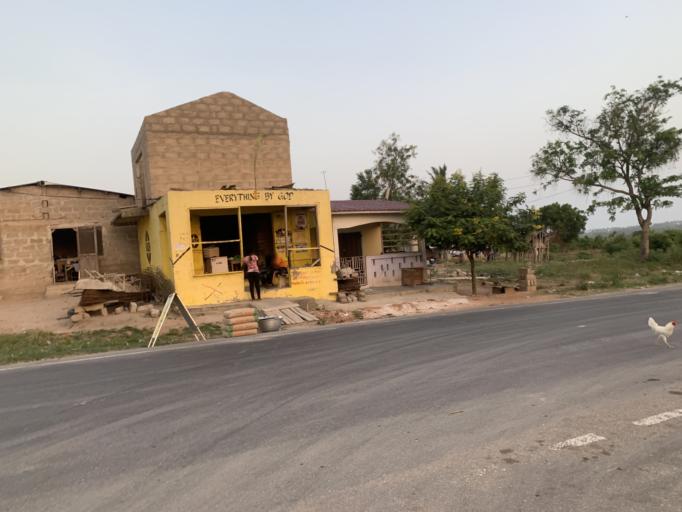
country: GH
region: Central
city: Winneba
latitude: 5.3757
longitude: -0.6067
